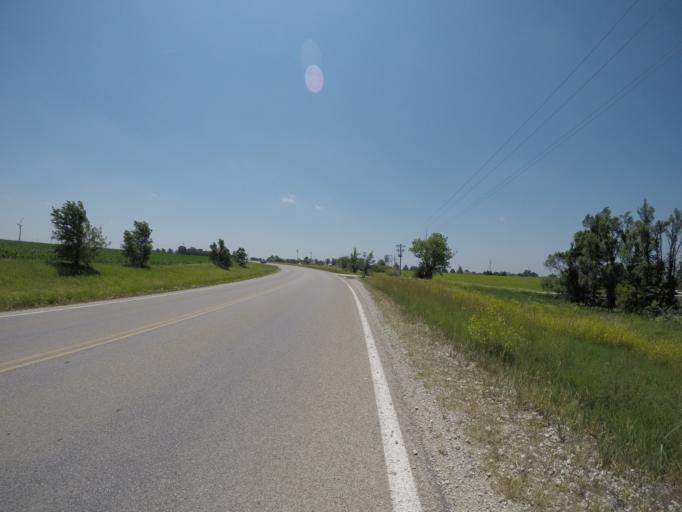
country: US
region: Kansas
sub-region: Riley County
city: Manhattan
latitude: 39.2347
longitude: -96.4454
